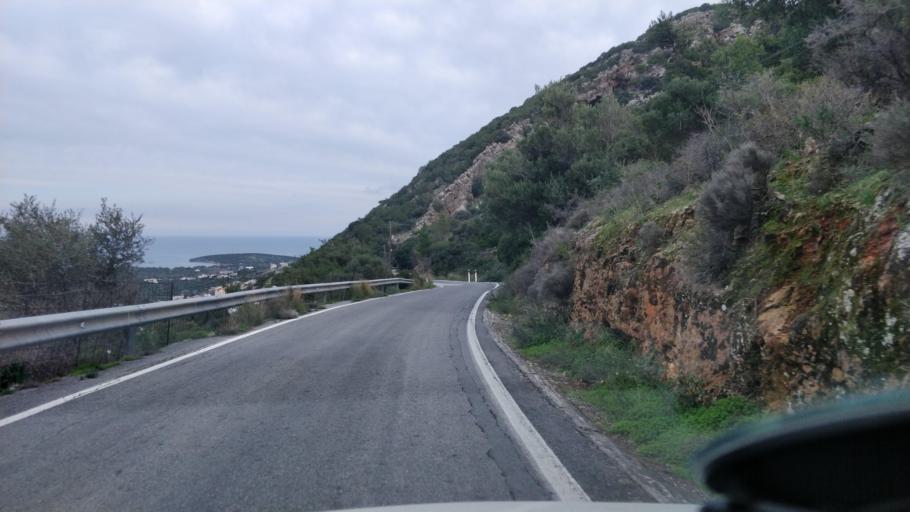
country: GR
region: Crete
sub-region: Nomos Lasithiou
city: Agios Nikolaos
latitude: 35.1080
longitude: 25.7138
